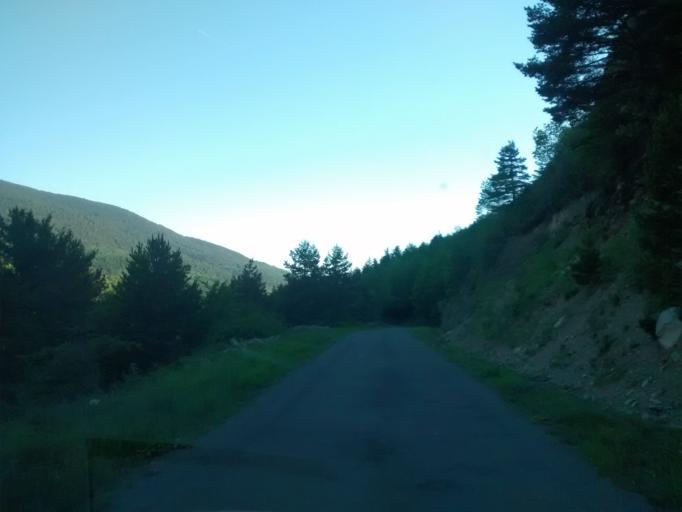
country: ES
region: Aragon
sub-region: Provincia de Huesca
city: Canfranc
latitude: 42.7339
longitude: -0.5947
